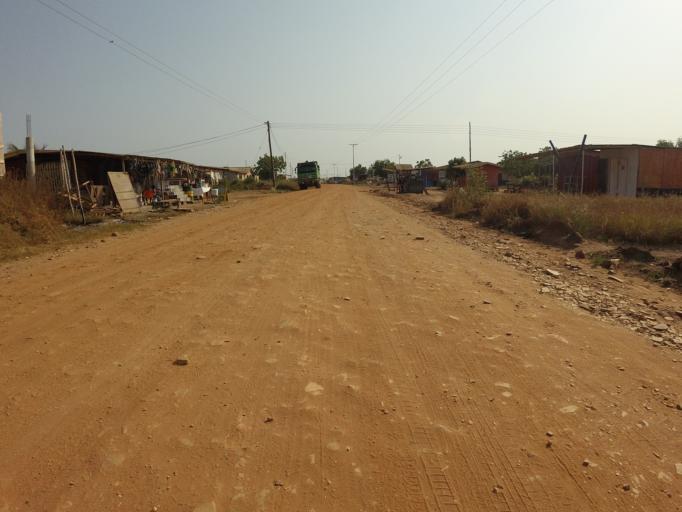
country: GH
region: Greater Accra
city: Tema
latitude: 5.7062
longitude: 0.0574
